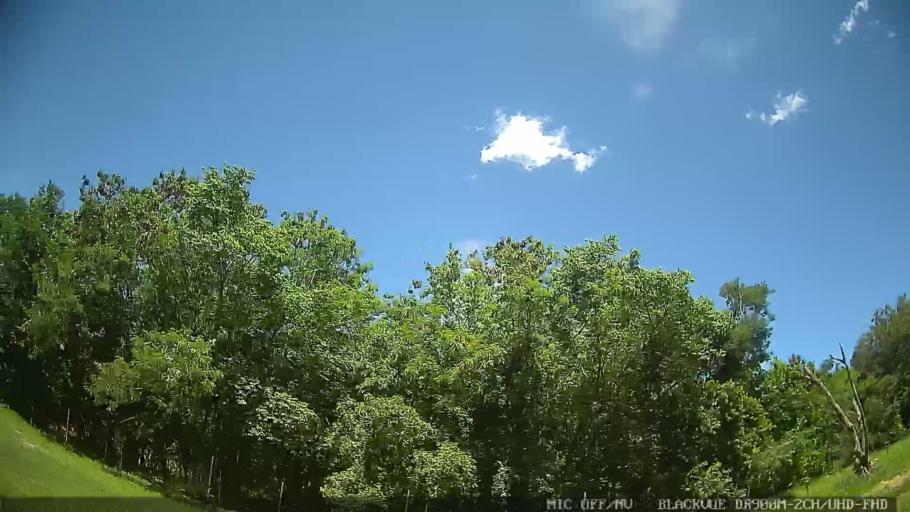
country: BR
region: Sao Paulo
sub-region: Pedreira
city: Pedreira
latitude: -22.7520
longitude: -46.9159
